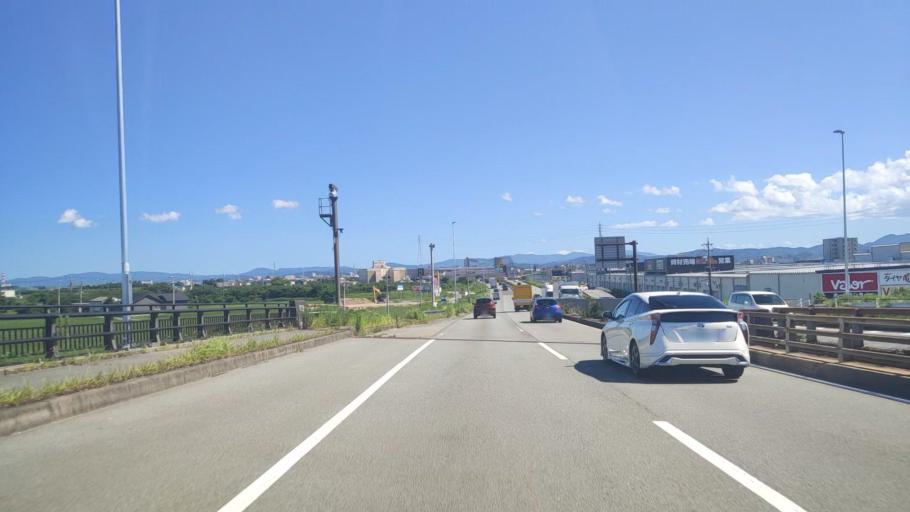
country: JP
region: Mie
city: Hisai-motomachi
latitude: 34.6111
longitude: 136.5187
